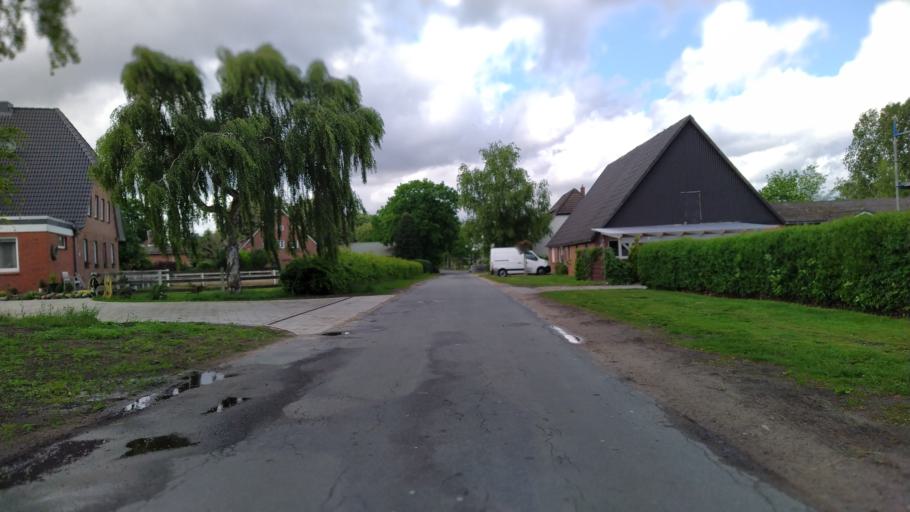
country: DE
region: Lower Saxony
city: Brest
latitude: 53.4495
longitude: 9.3823
